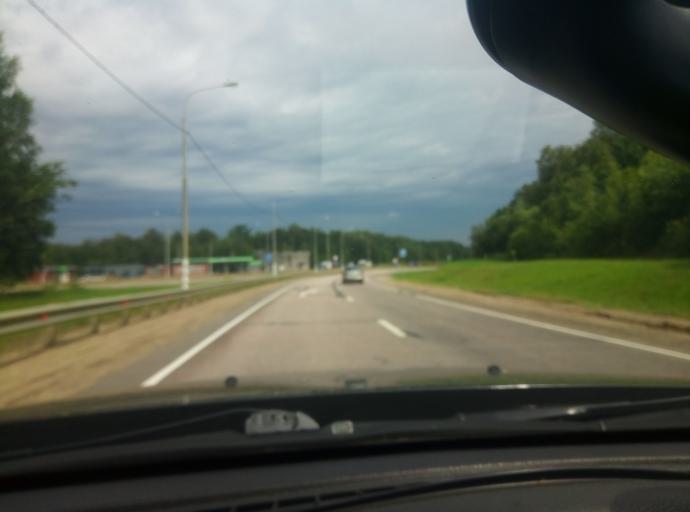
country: RU
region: Tula
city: Leninskiy
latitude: 54.4125
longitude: 37.5009
